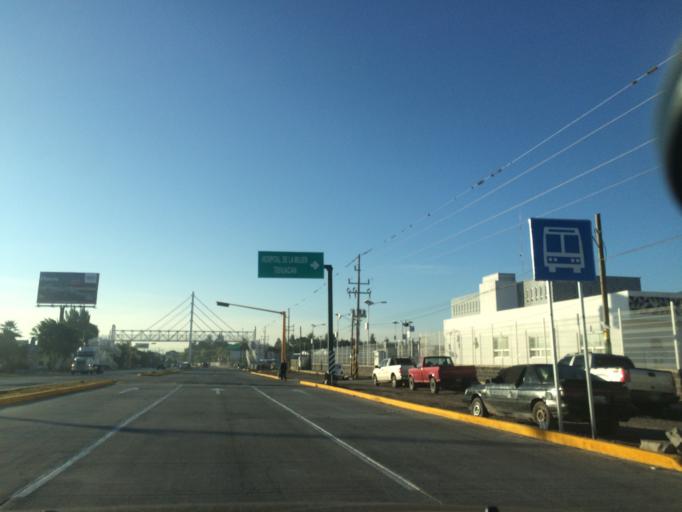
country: MX
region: Puebla
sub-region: Santiago Miahuatlan
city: San Jose Monte Chiquito
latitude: 18.4775
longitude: -97.4396
